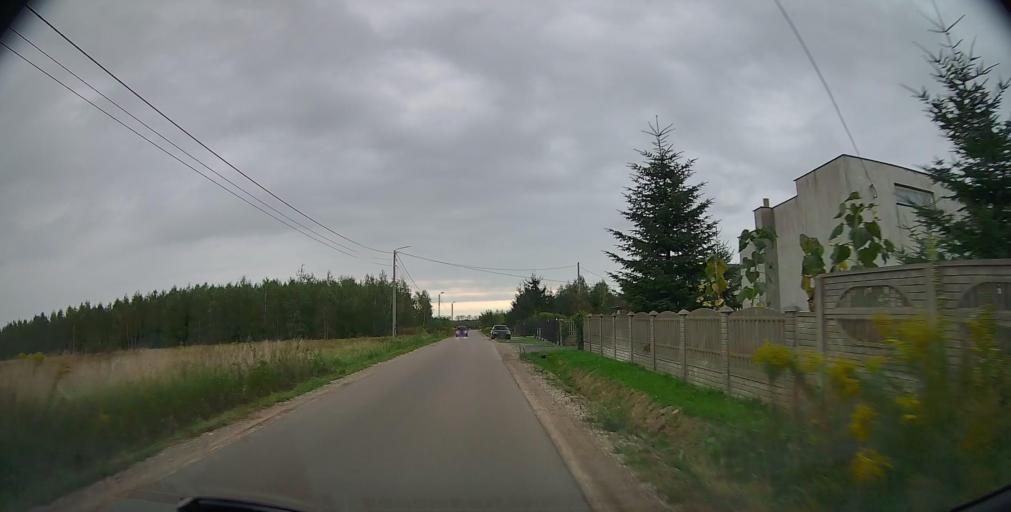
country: PL
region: Masovian Voivodeship
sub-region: Powiat radomski
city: Jedlinsk
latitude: 51.4519
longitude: 21.0992
